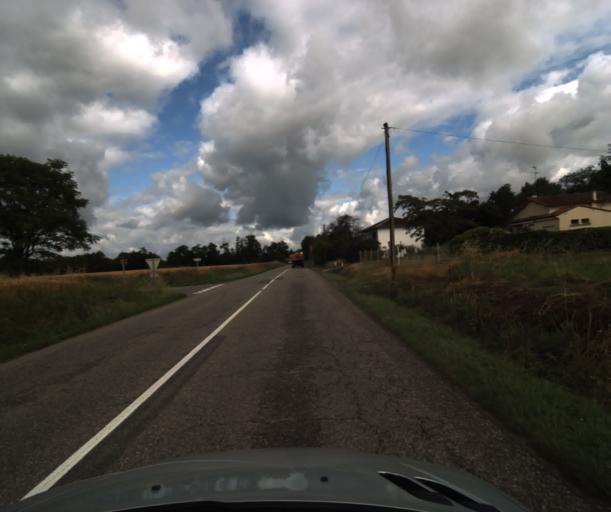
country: FR
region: Midi-Pyrenees
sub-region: Departement du Tarn-et-Garonne
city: Castelsarrasin
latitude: 44.0238
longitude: 1.0626
